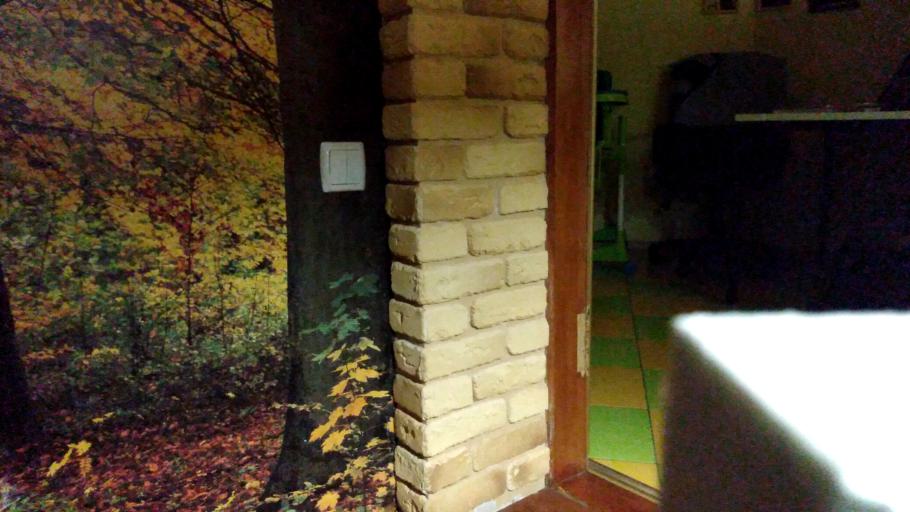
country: RU
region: Vologda
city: Lipin Bor
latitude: 60.8361
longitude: 38.0201
